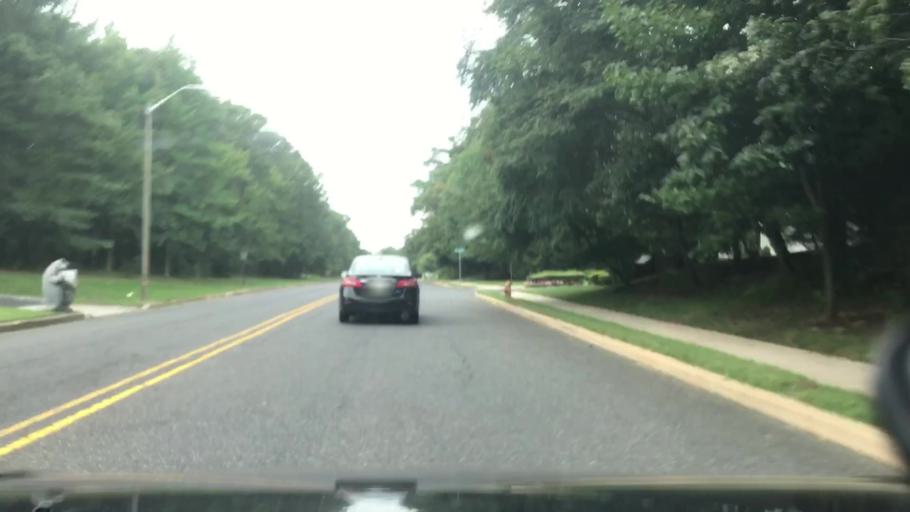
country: US
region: New Jersey
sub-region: Monmouth County
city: Eatontown
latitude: 40.2887
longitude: -74.0395
